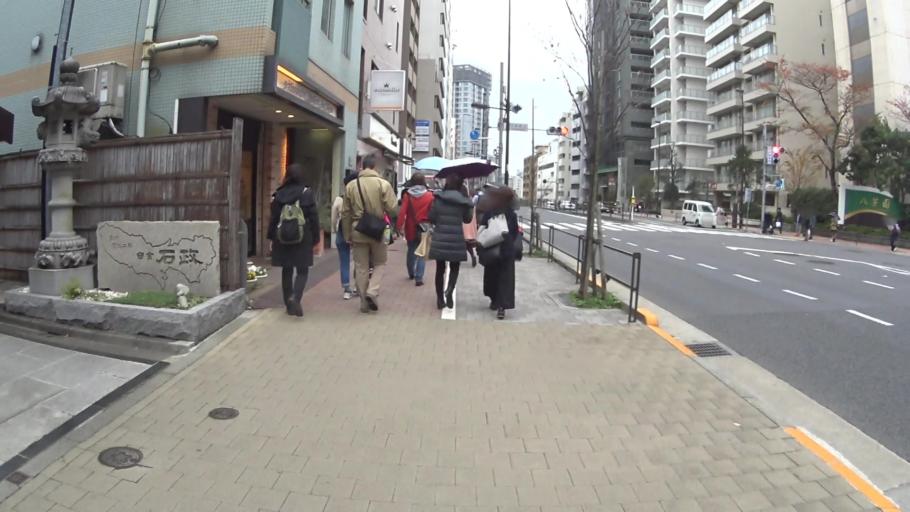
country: JP
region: Tokyo
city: Tokyo
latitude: 35.6385
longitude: 139.7270
